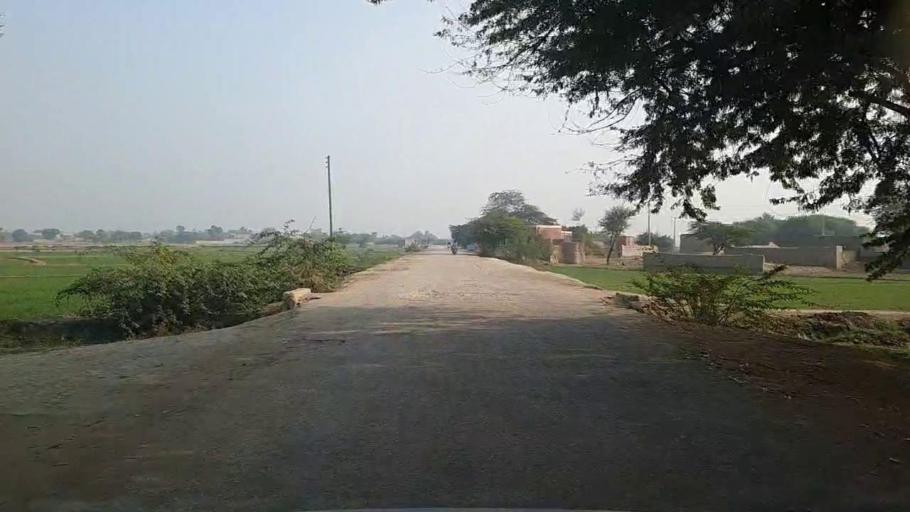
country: PK
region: Sindh
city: Kandiari
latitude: 27.0455
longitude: 68.4725
